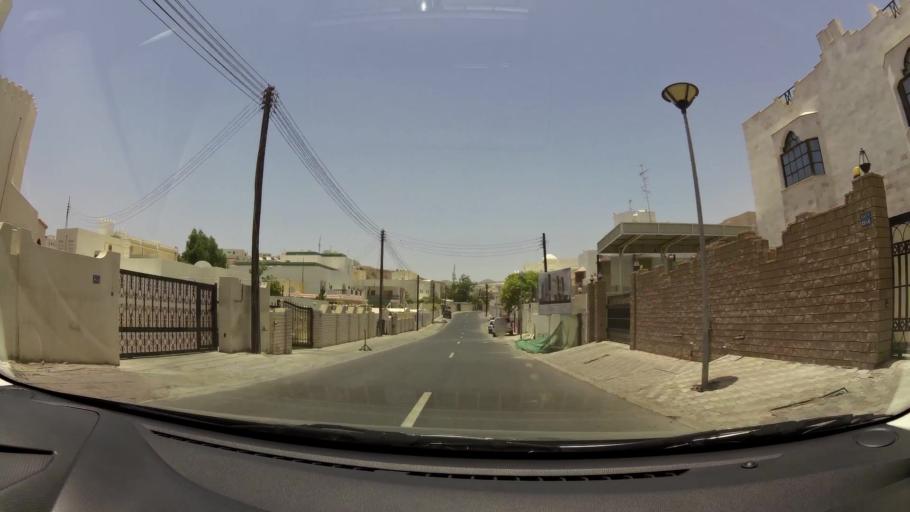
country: OM
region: Muhafazat Masqat
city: Bawshar
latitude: 23.6041
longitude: 58.4617
